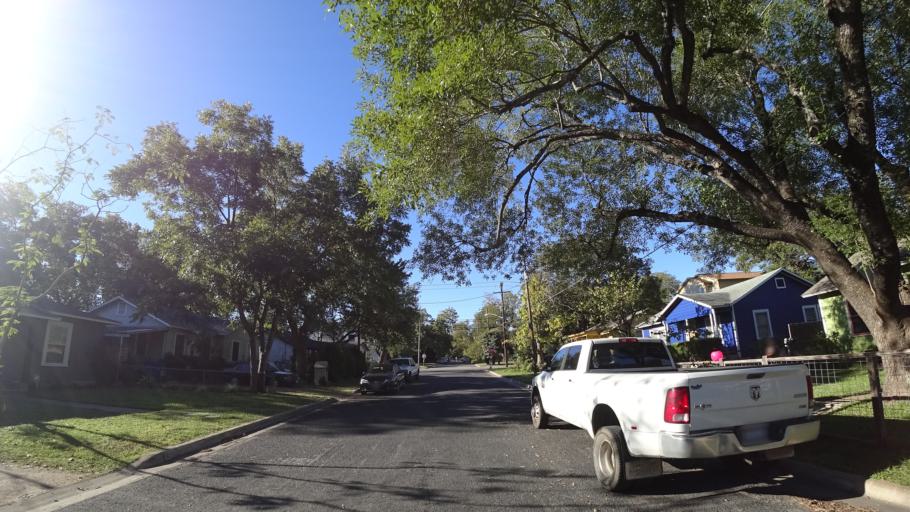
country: US
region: Texas
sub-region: Travis County
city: Austin
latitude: 30.2382
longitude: -97.7610
